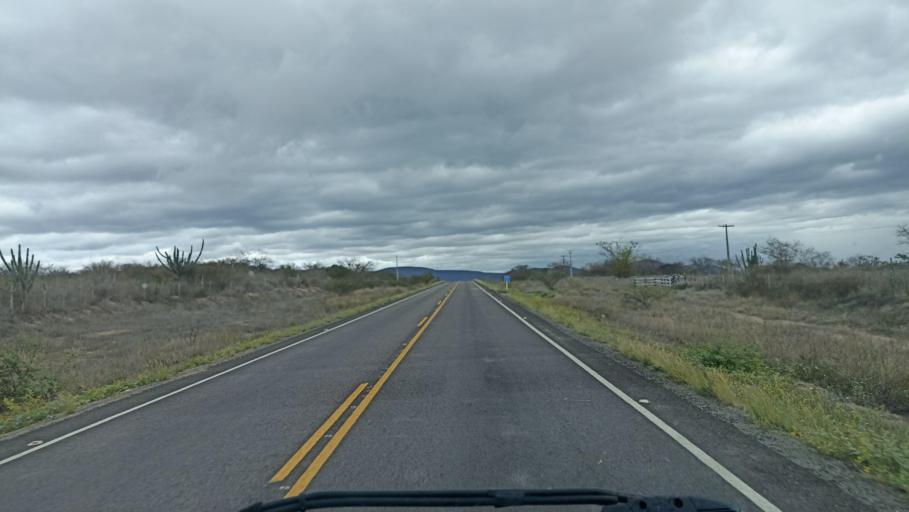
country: BR
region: Bahia
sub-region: Iacu
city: Iacu
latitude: -12.9100
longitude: -40.4080
